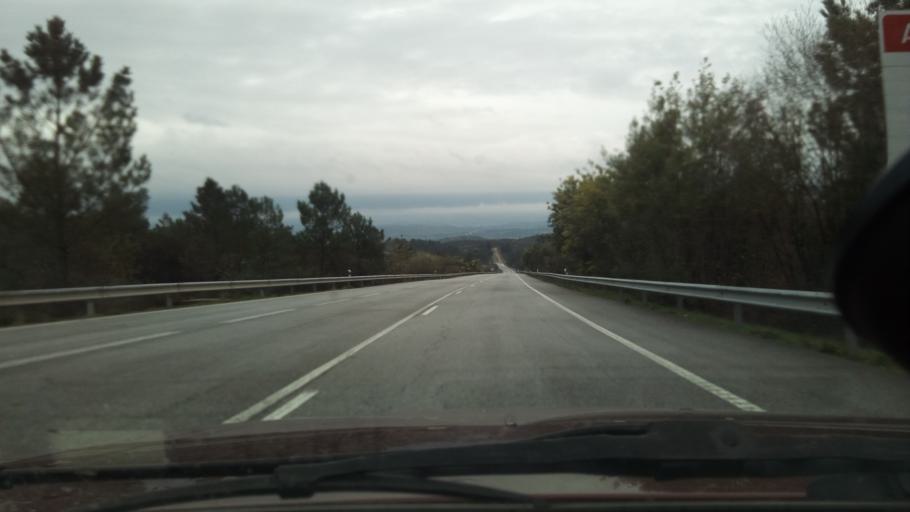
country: PT
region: Guarda
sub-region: Fornos de Algodres
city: Fornos de Algodres
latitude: 40.6115
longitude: -7.5936
